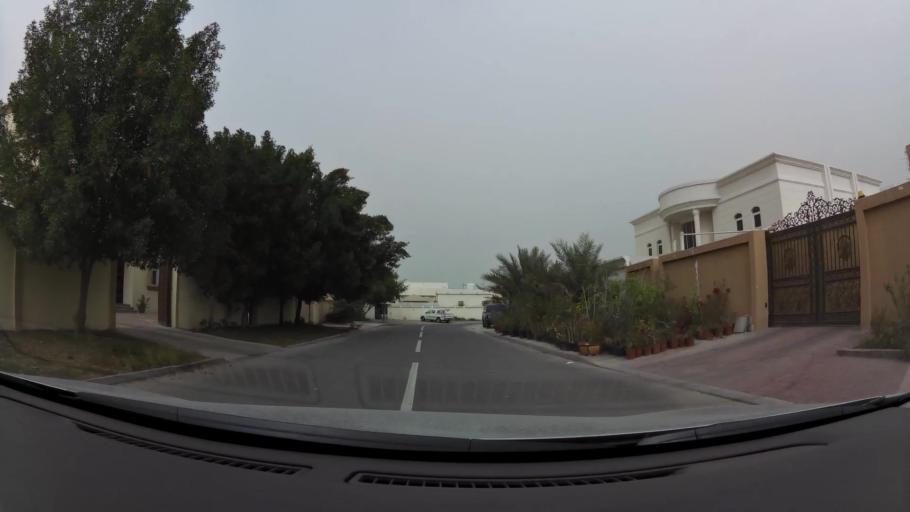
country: QA
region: Baladiyat ad Dawhah
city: Doha
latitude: 25.2497
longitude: 51.5131
